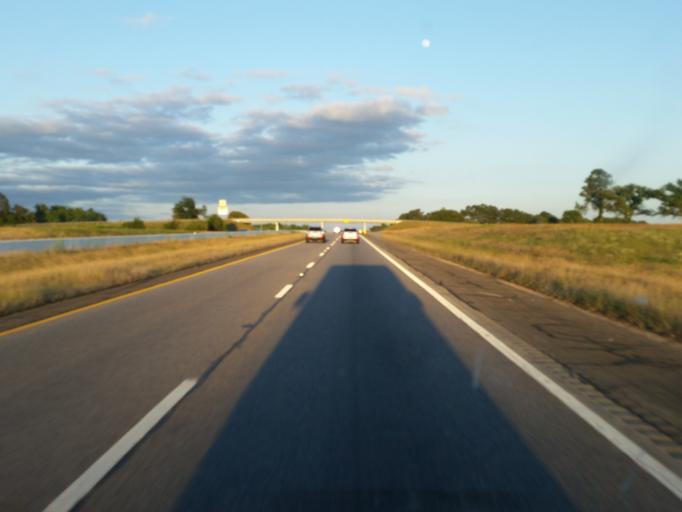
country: US
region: Texas
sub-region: Van Zandt County
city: Canton
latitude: 32.5435
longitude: -95.7605
